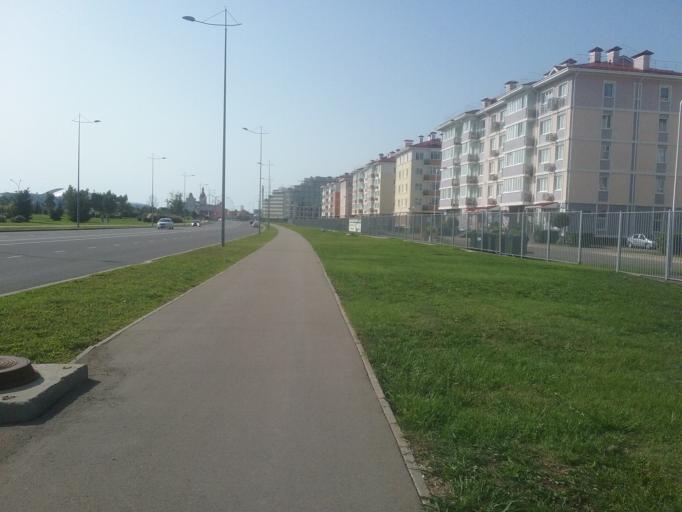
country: RU
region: Krasnodarskiy
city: Adler
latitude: 43.3993
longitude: 39.9812
